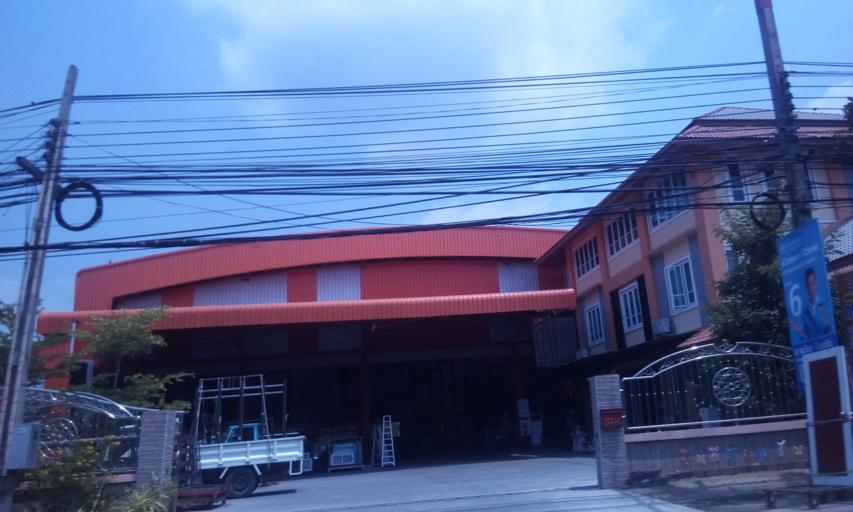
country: TH
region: Chachoengsao
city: Chachoengsao
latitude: 13.6736
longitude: 101.0842
